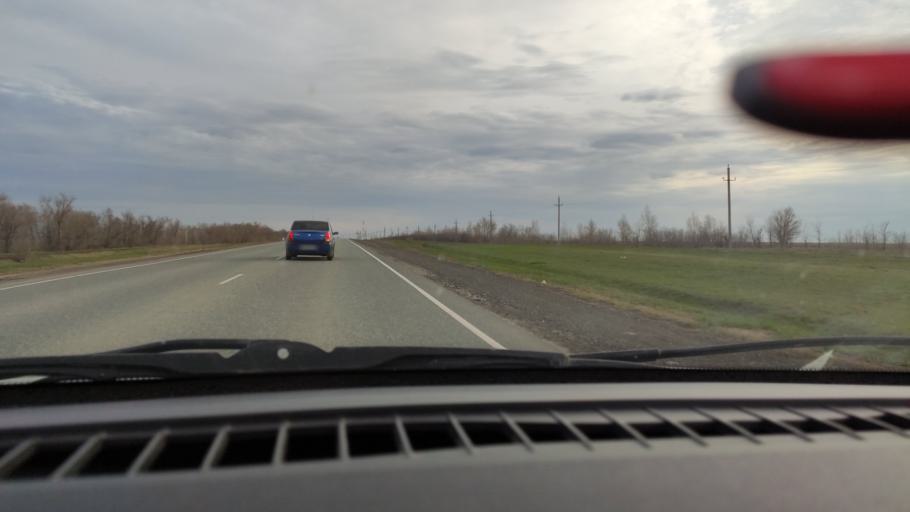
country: RU
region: Orenburg
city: Tatarskaya Kargala
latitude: 51.9958
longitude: 55.1949
